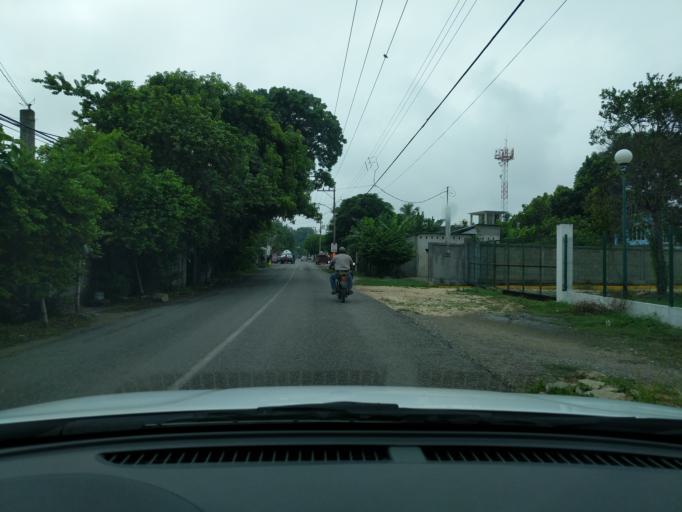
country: MX
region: Tabasco
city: Villahermosa
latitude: 17.9561
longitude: -92.9649
